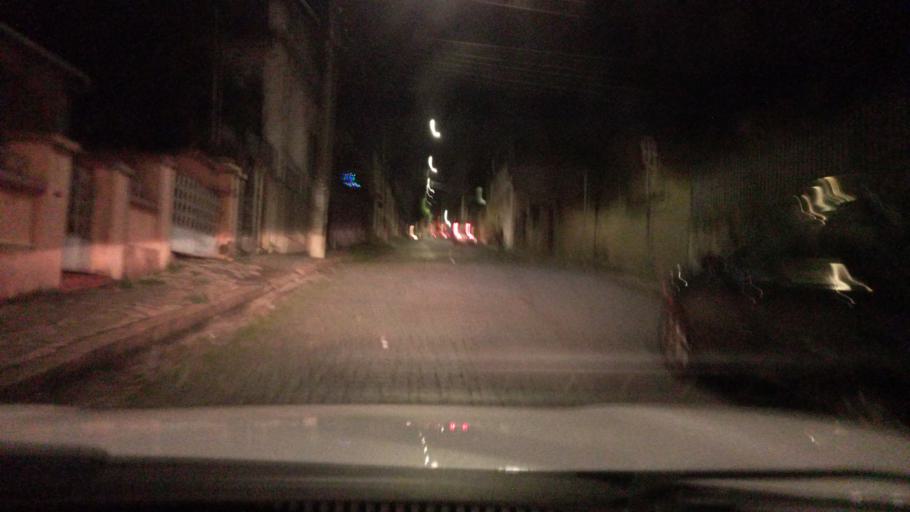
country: BR
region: Minas Gerais
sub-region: Belo Horizonte
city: Belo Horizonte
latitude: -19.9075
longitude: -43.9463
